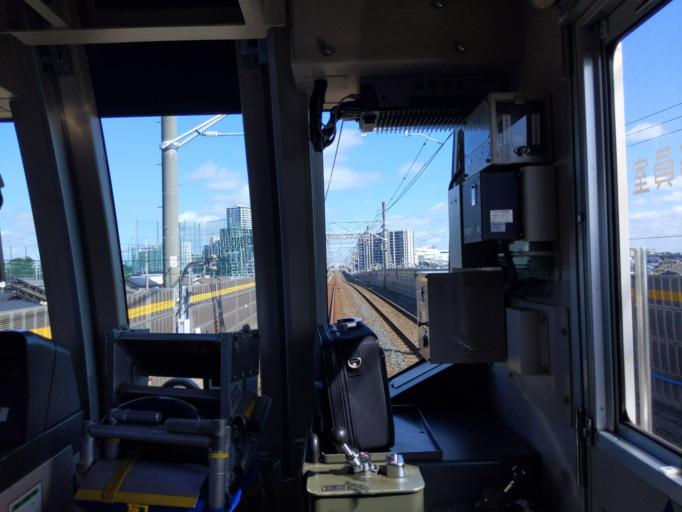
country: JP
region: Chiba
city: Shiroi
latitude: 35.7283
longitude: 140.0650
